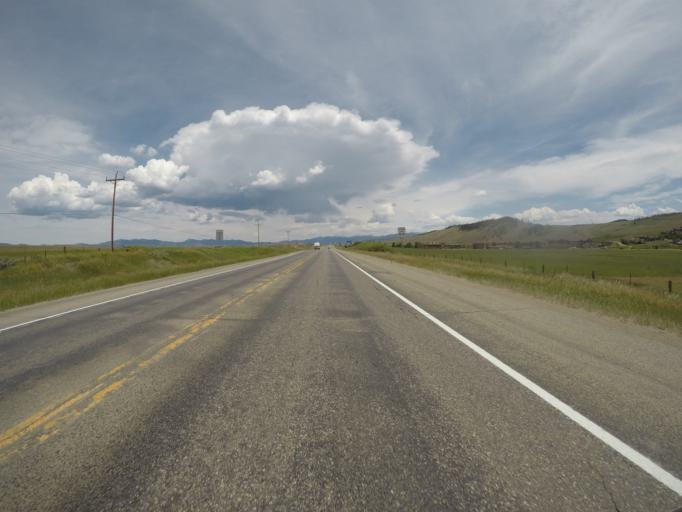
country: US
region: Colorado
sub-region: Grand County
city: Granby
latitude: 40.0572
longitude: -105.9292
